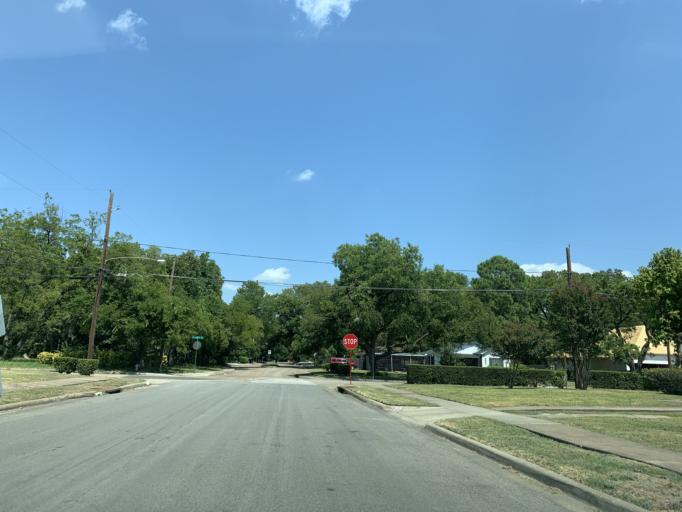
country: US
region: Texas
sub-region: Dallas County
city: Hutchins
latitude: 32.7024
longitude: -96.7650
